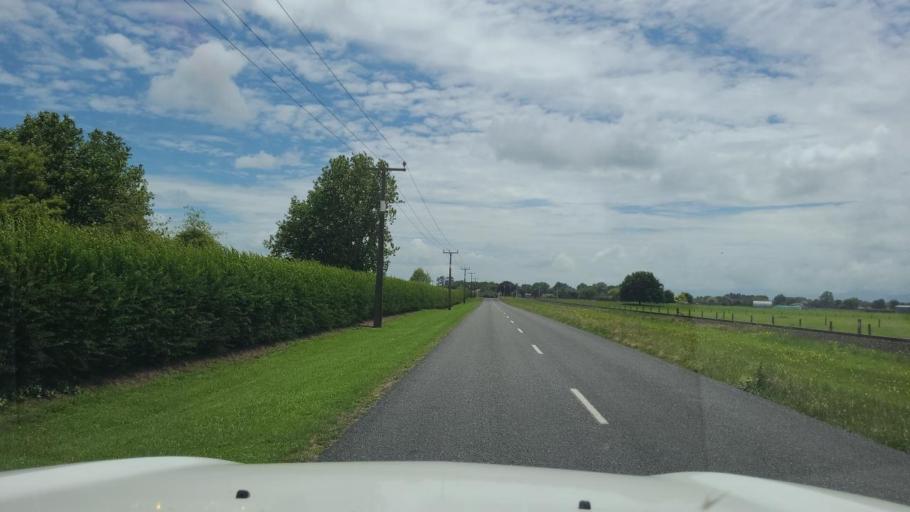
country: NZ
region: Waikato
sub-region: Matamata-Piako District
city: Matamata
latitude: -37.8670
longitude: 175.7556
